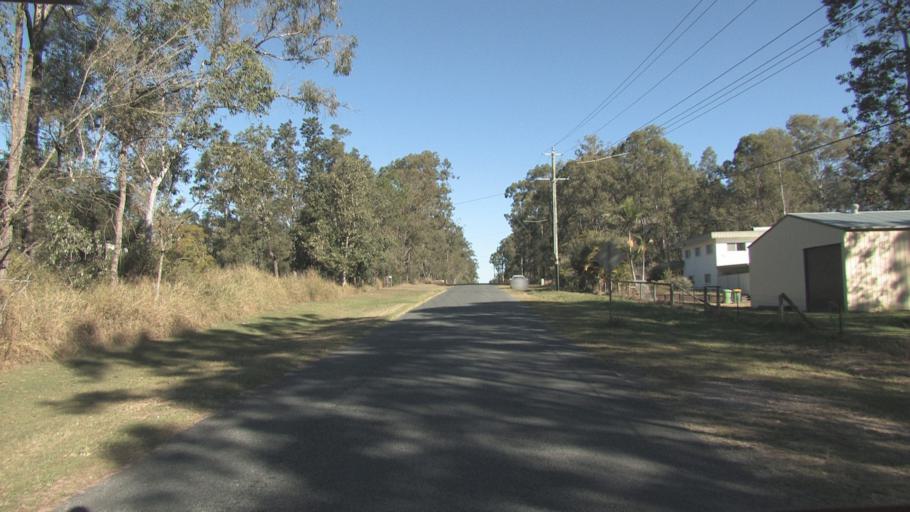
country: AU
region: Queensland
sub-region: Logan
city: Park Ridge South
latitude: -27.7253
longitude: 153.0124
